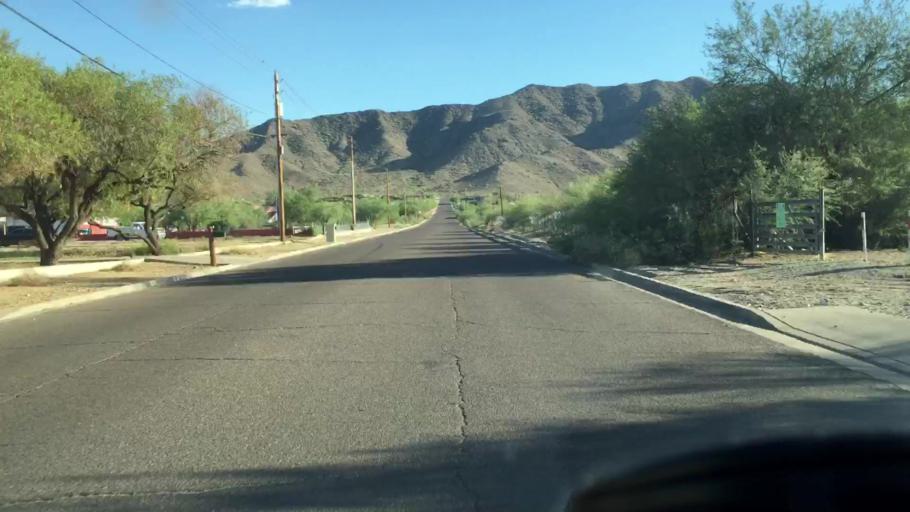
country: US
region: Arizona
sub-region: Maricopa County
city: Laveen
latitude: 33.3653
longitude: -112.0989
